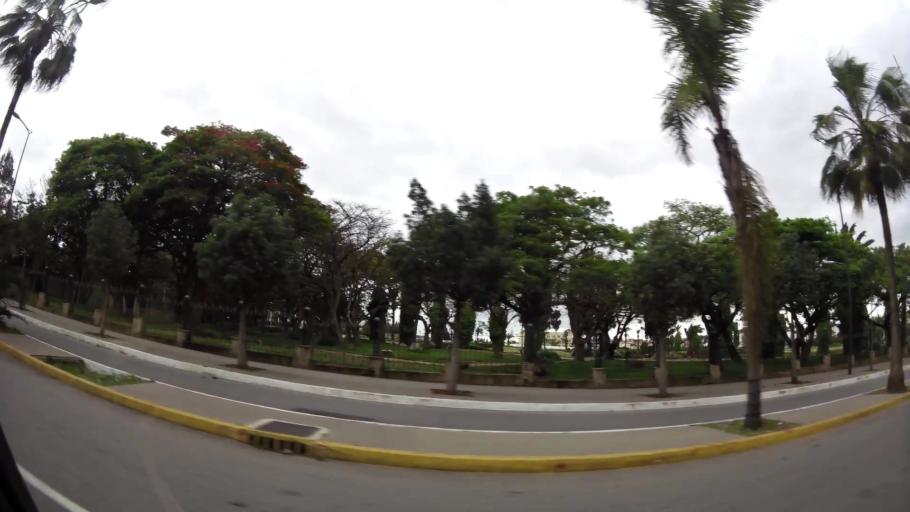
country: MA
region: Grand Casablanca
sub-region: Casablanca
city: Casablanca
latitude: 33.5589
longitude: -7.5614
